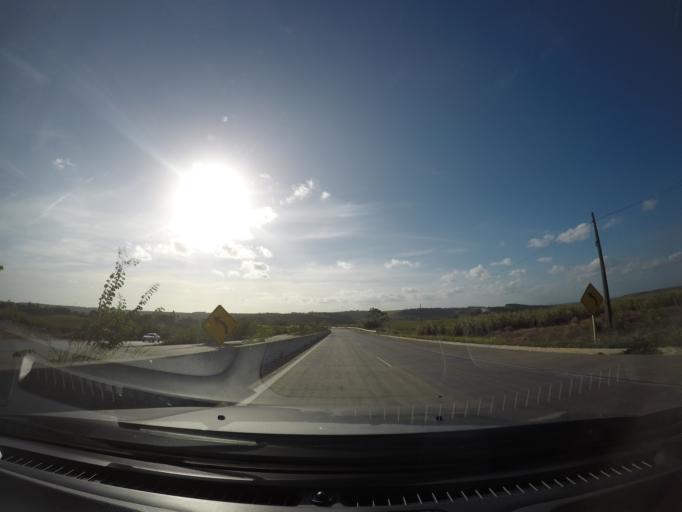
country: BR
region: Alagoas
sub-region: Pilar
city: Pilar
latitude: -9.5859
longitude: -35.9981
